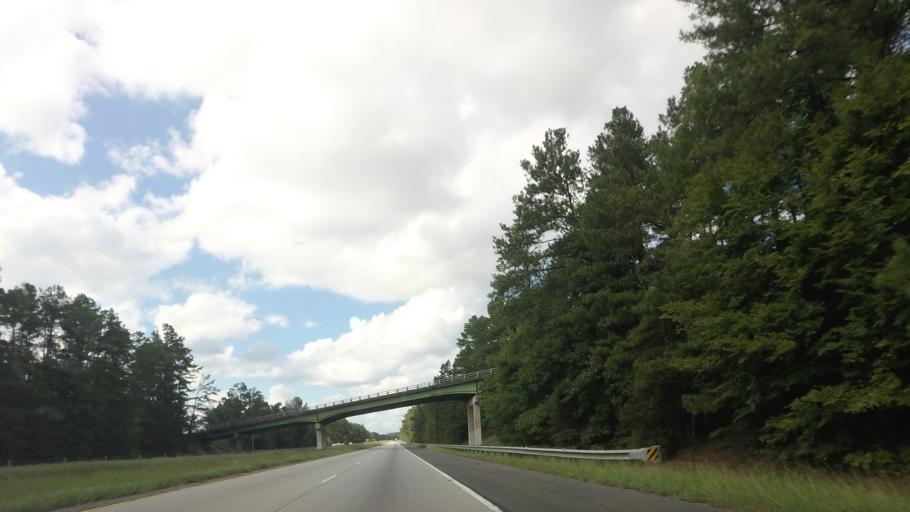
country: US
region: Georgia
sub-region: Bibb County
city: Macon
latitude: 32.7729
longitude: -83.5575
